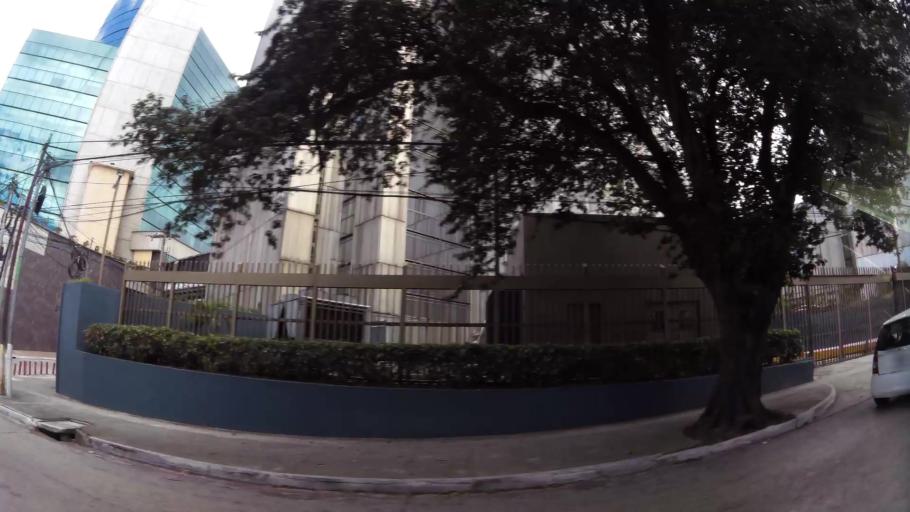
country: GT
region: Guatemala
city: Guatemala City
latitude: 14.6187
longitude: -90.5167
